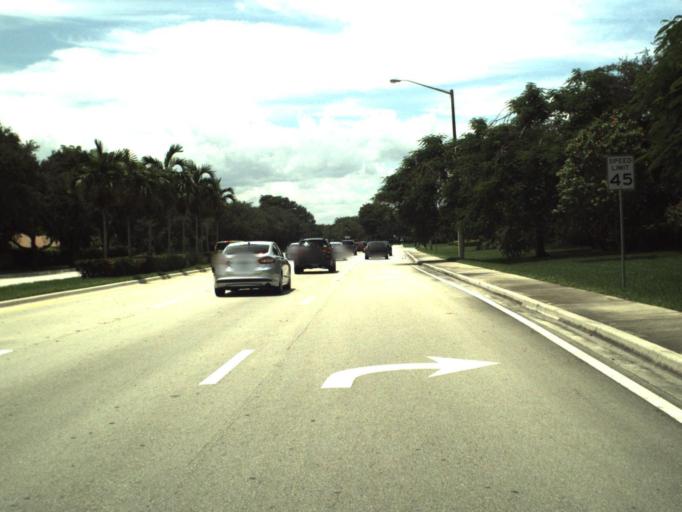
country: US
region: Florida
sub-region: Broward County
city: Coral Springs
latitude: 26.2409
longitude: -80.2700
